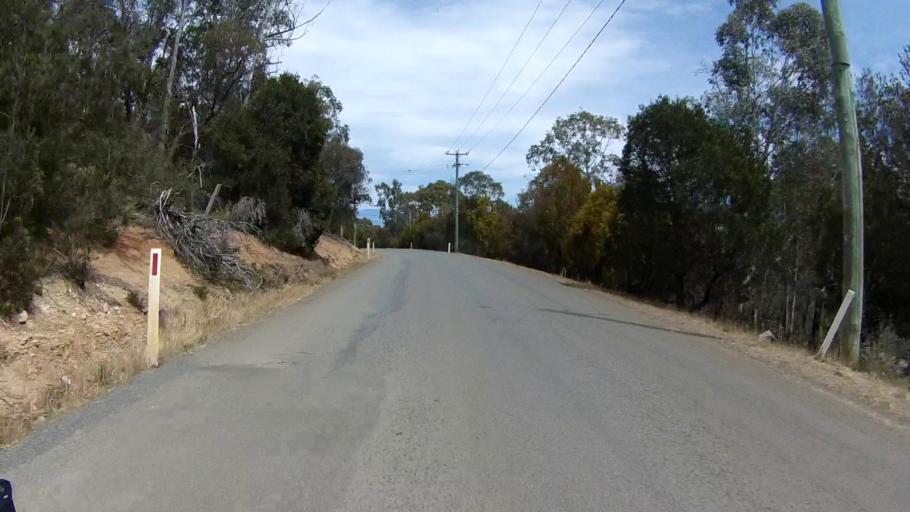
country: AU
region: Tasmania
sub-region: Sorell
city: Sorell
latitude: -42.8004
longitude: 147.6794
